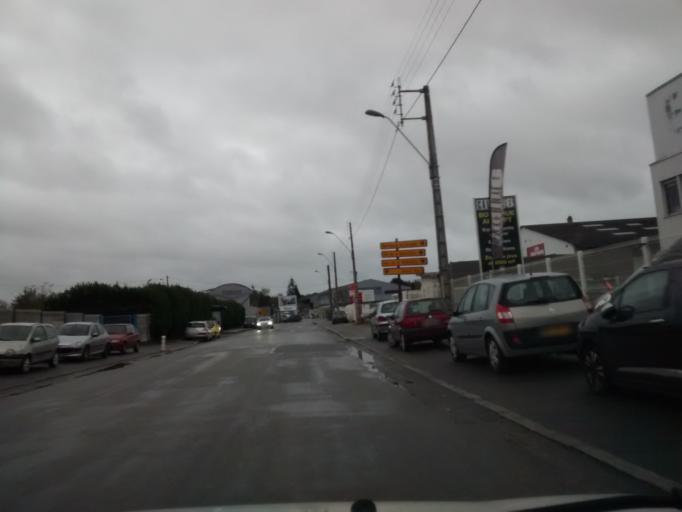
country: FR
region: Brittany
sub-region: Departement d'Ille-et-Vilaine
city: Vezin-le-Coquet
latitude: 48.1042
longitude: -1.7236
